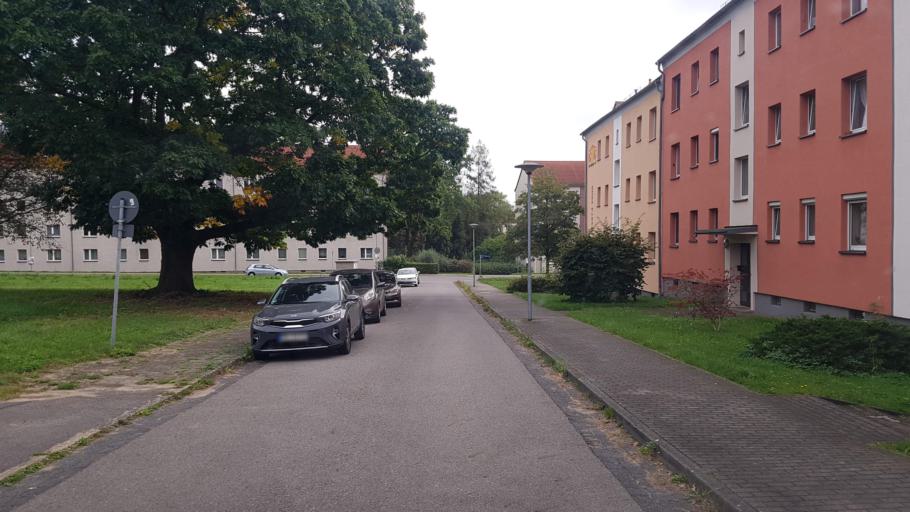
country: DE
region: Brandenburg
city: Lauchhammer
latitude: 51.5003
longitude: 13.7662
